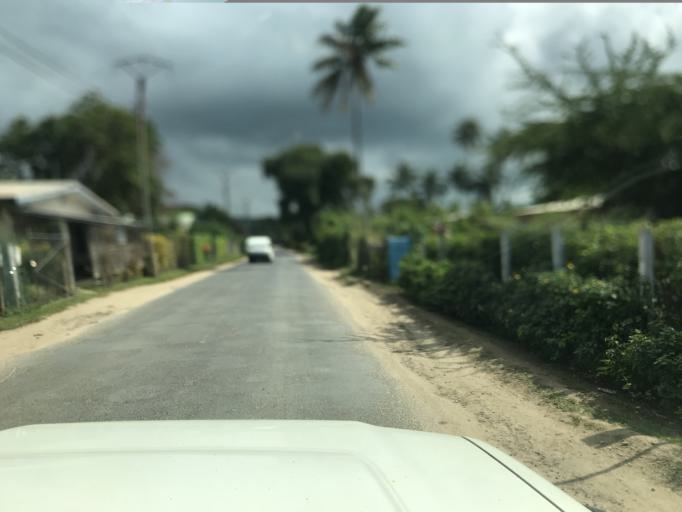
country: VU
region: Sanma
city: Luganville
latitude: -15.5123
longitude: 167.1769
